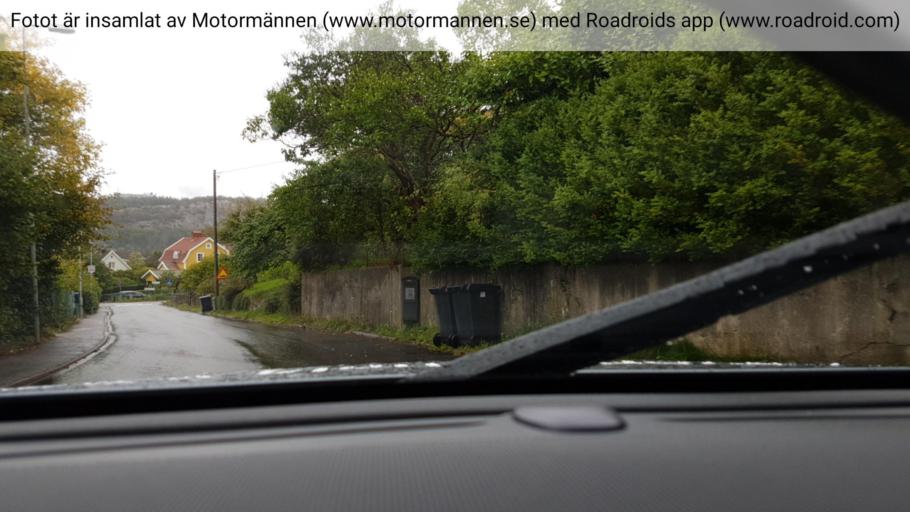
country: SE
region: Vaestra Goetaland
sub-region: Molndal
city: Moelndal
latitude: 57.6727
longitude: 11.9976
